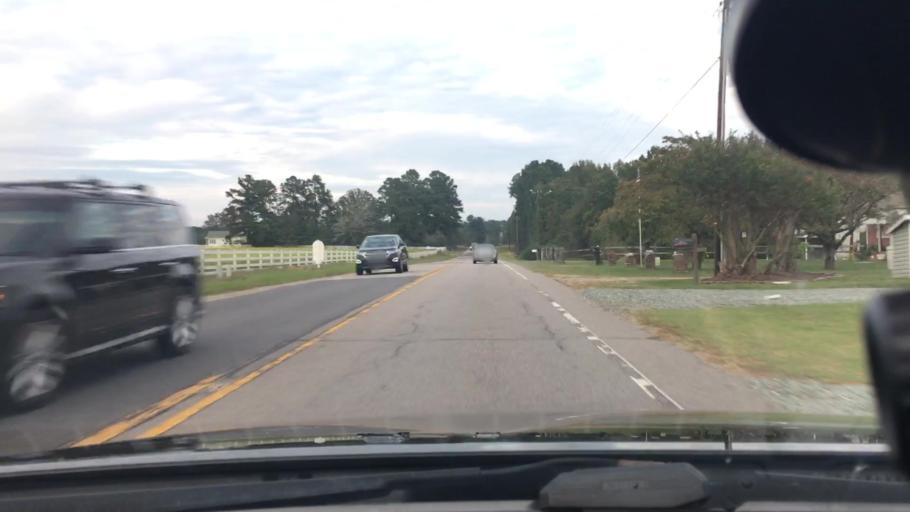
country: US
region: North Carolina
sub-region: Moore County
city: Carthage
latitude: 35.3632
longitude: -79.3188
